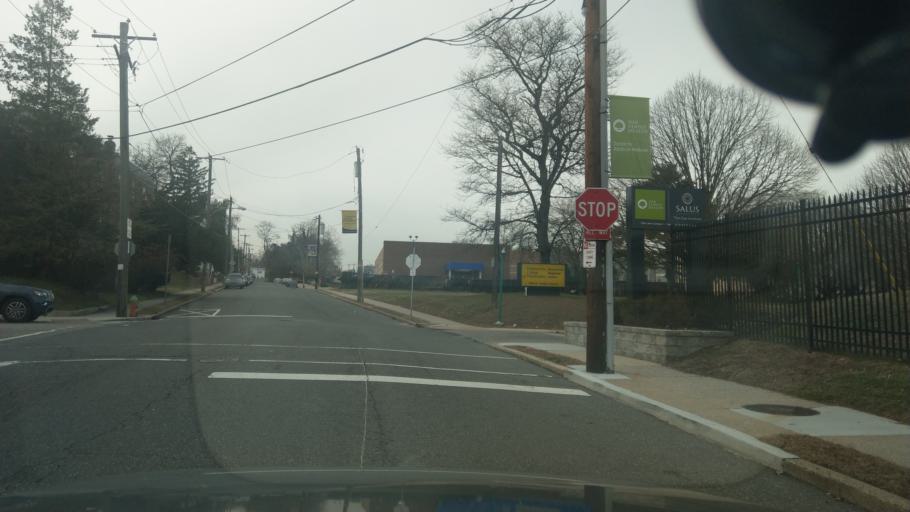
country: US
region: Pennsylvania
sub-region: Montgomery County
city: Wyncote
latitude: 40.0457
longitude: -75.1408
